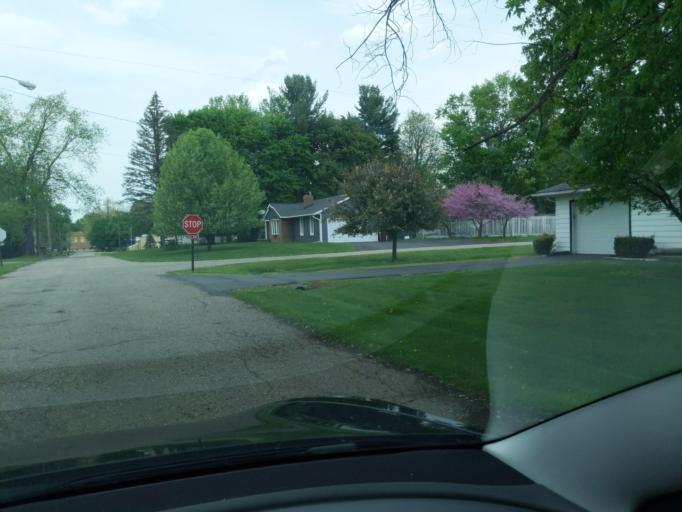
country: US
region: Michigan
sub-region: Ingham County
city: Stockbridge
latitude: 42.4464
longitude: -84.1825
